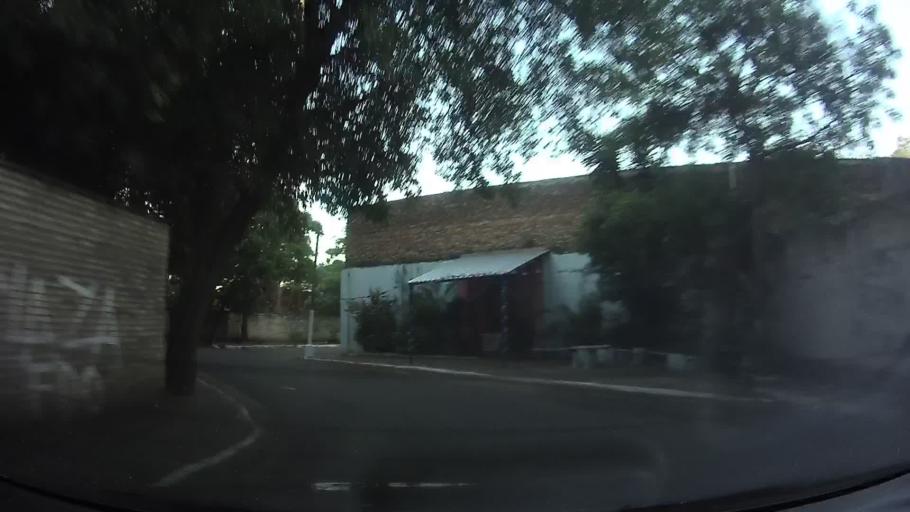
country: PY
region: Central
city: Fernando de la Mora
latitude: -25.3306
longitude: -57.5454
